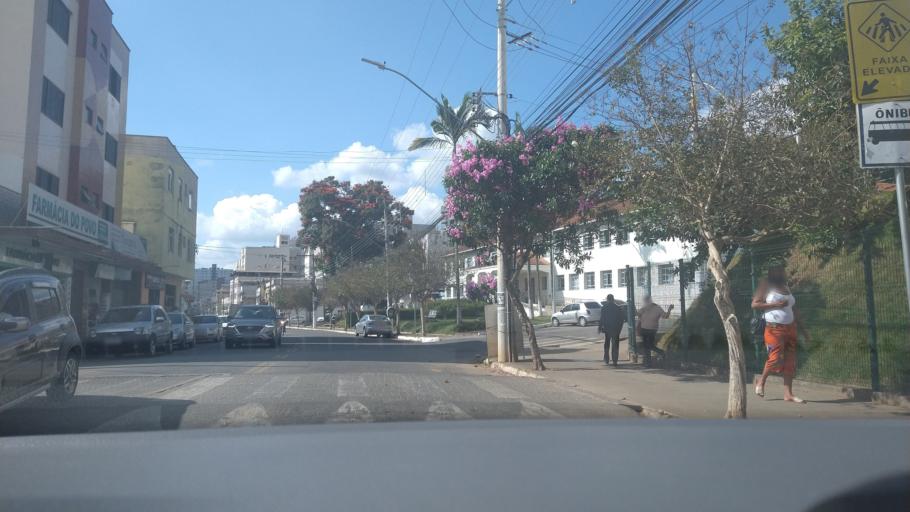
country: BR
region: Minas Gerais
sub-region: Vicosa
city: Vicosa
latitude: -20.7640
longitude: -42.8817
